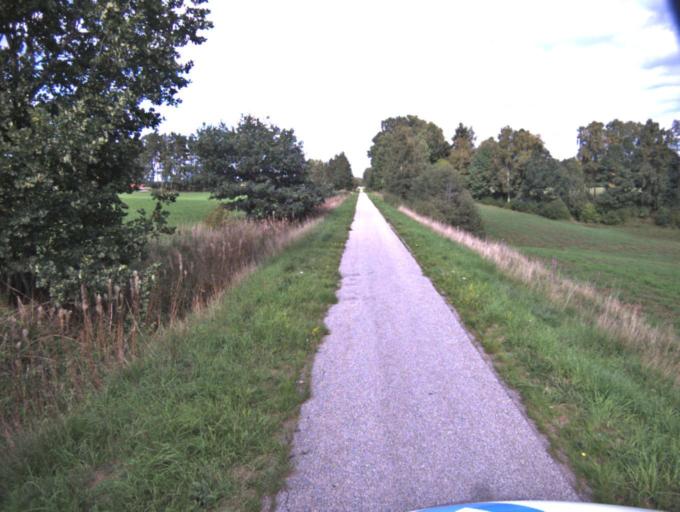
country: SE
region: Vaestra Goetaland
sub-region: Ulricehamns Kommun
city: Ulricehamn
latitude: 57.8484
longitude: 13.4245
